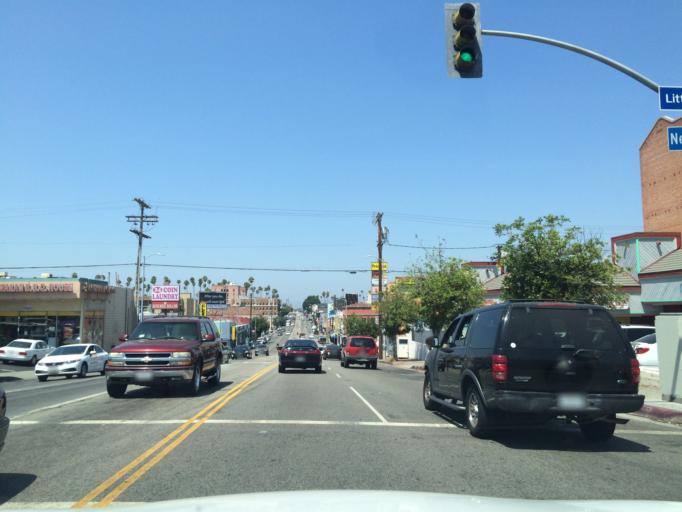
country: US
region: California
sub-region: Los Angeles County
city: Silver Lake
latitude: 34.0691
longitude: -118.2929
